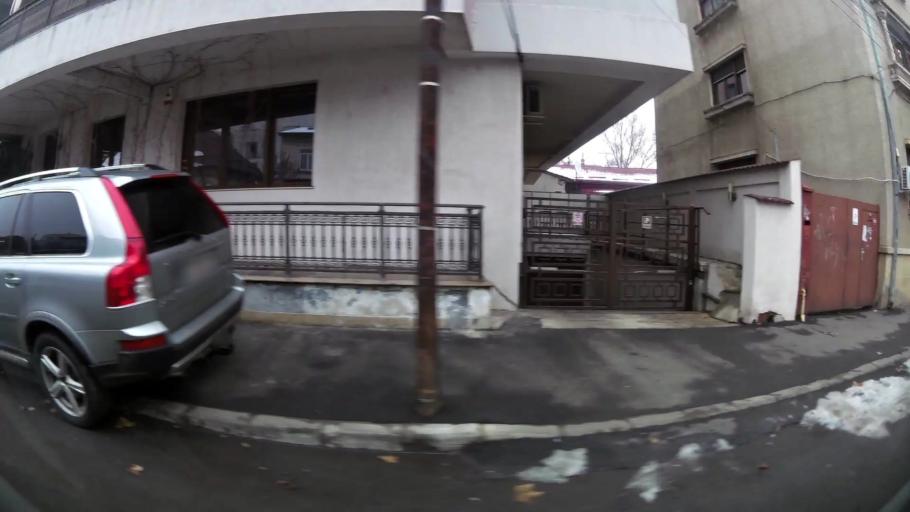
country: RO
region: Bucuresti
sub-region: Municipiul Bucuresti
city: Bucharest
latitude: 44.4494
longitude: 26.1097
